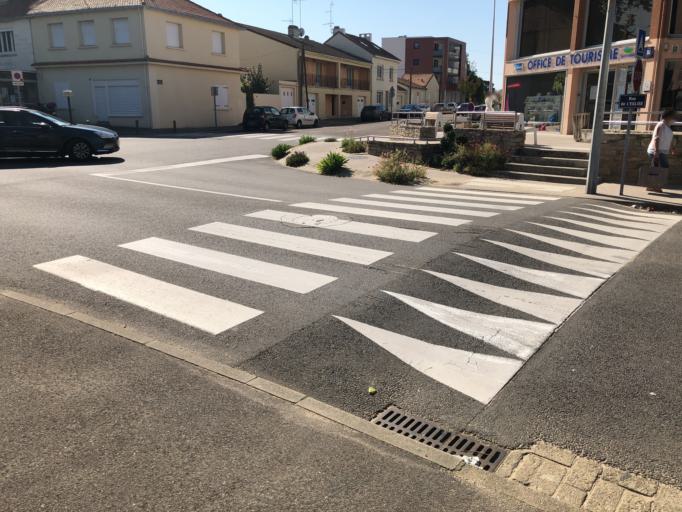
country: FR
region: Pays de la Loire
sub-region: Departement de la Loire-Atlantique
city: Saint-Brevin-les-Pins
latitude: 47.2474
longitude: -2.1686
